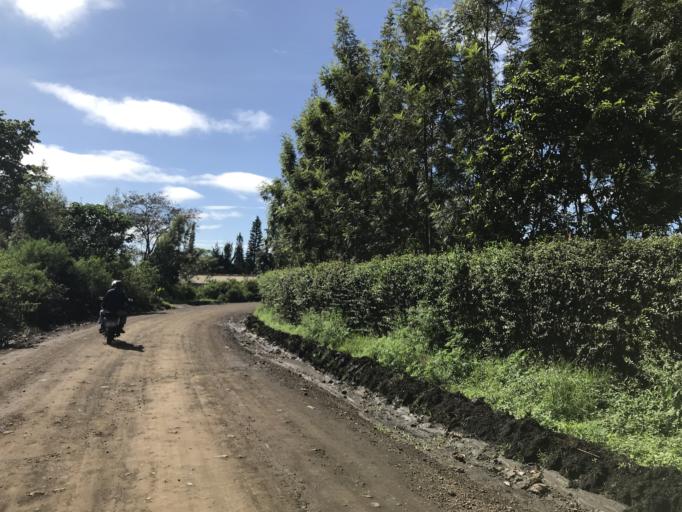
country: TZ
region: Arusha
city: Nkoaranga
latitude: -3.3822
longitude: 36.7951
